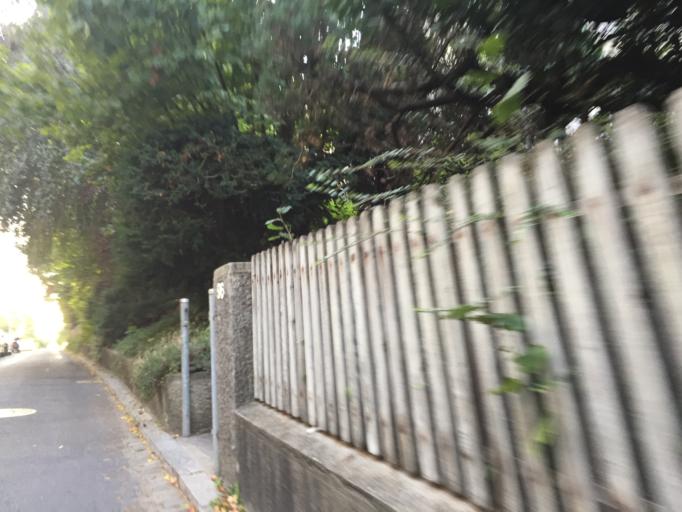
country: CH
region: Bern
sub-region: Bern-Mittelland District
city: Bern
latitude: 46.9587
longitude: 7.4334
